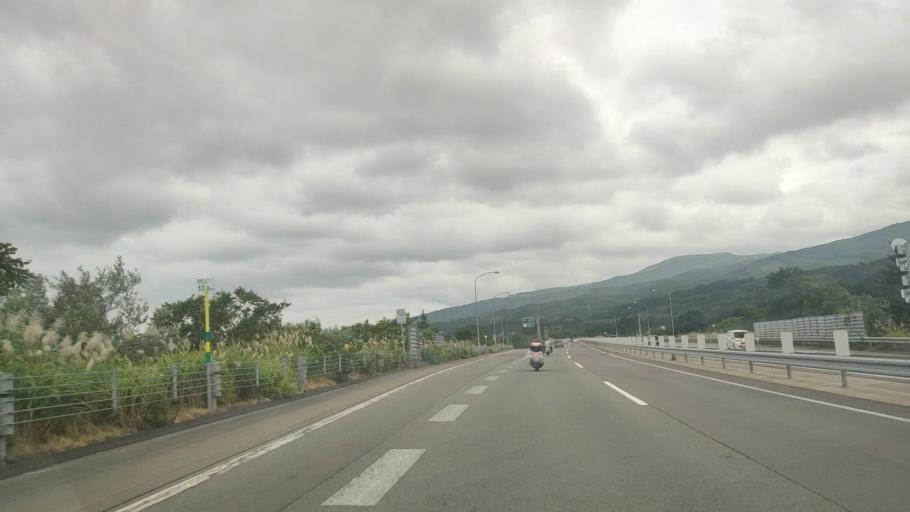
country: JP
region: Hokkaido
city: Nanae
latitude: 41.8650
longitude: 140.7305
